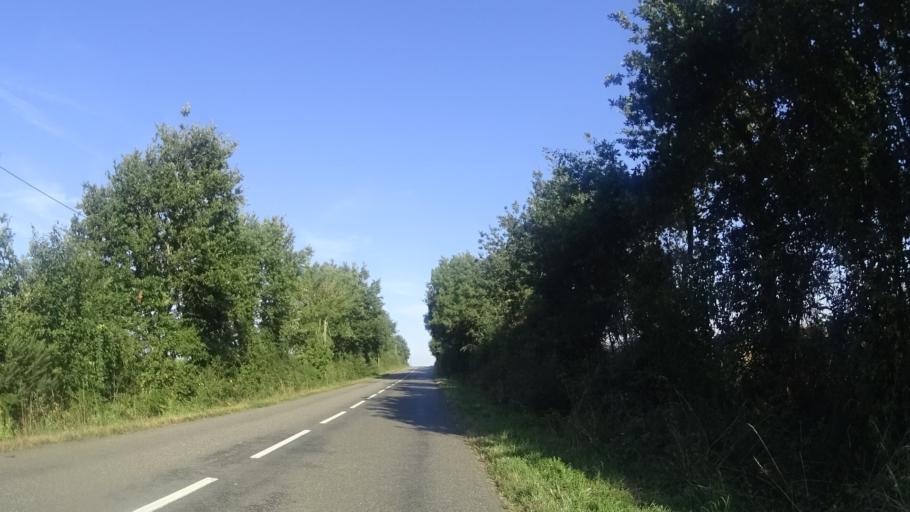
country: FR
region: Pays de la Loire
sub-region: Departement de la Loire-Atlantique
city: Joue-sur-Erdre
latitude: 47.4835
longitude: -1.3883
